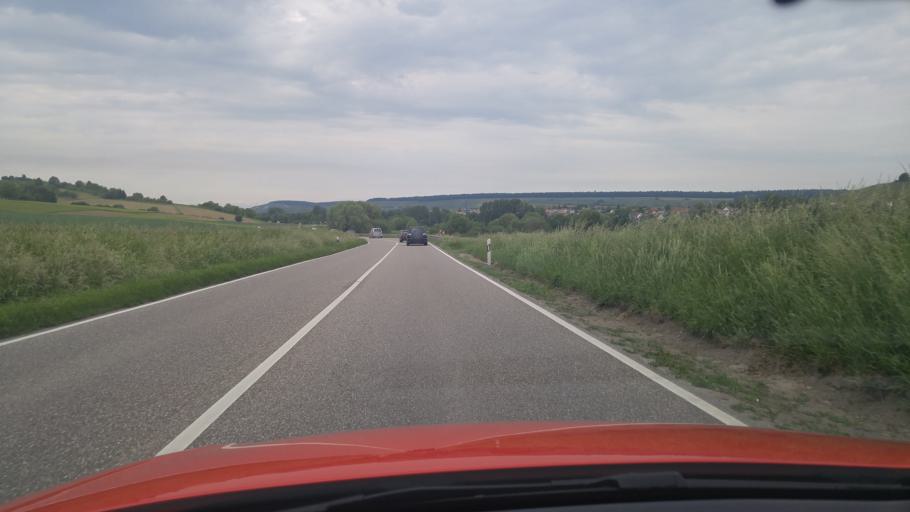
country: DE
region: Baden-Wuerttemberg
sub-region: Regierungsbezirk Stuttgart
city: Lehrensteinsfeld
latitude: 49.1392
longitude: 9.3508
